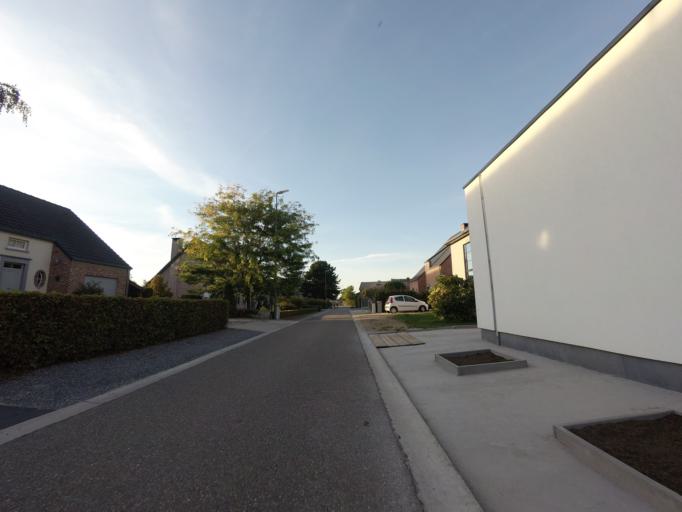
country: BE
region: Flanders
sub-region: Provincie Vlaams-Brabant
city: Boortmeerbeek
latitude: 50.9465
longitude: 4.6020
